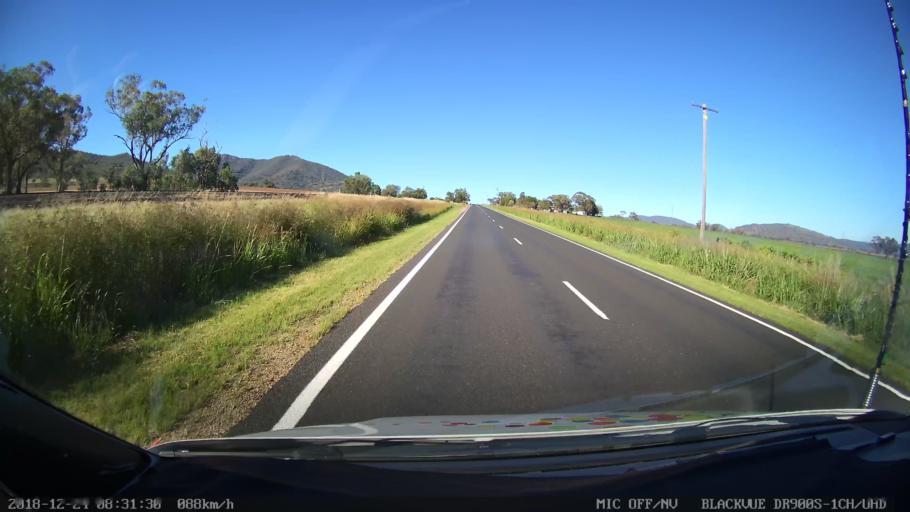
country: AU
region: New South Wales
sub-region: Tamworth Municipality
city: Phillip
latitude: -31.2739
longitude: 150.7107
